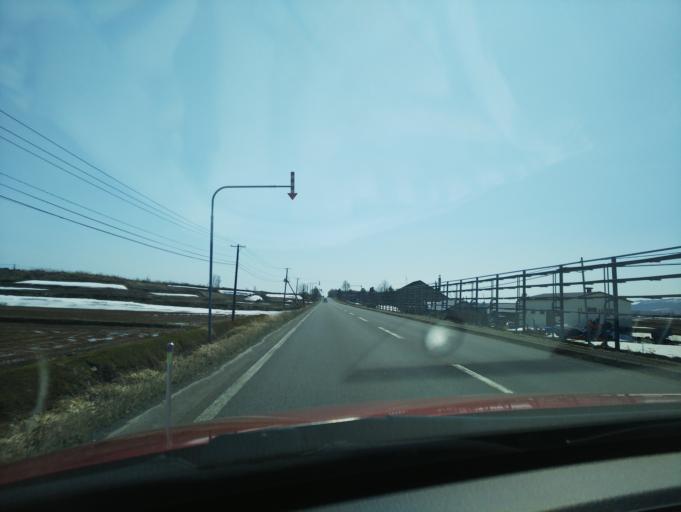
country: JP
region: Hokkaido
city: Nayoro
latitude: 44.2600
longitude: 142.3946
